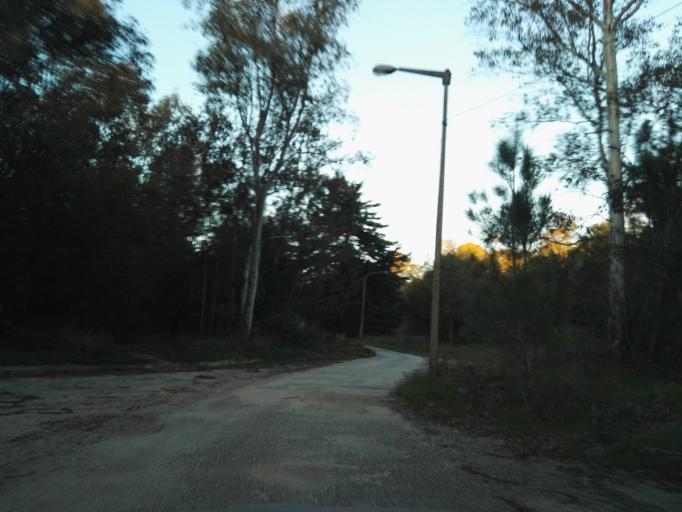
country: PT
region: Setubal
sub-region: Seixal
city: Corroios
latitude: 38.6189
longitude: -9.1468
